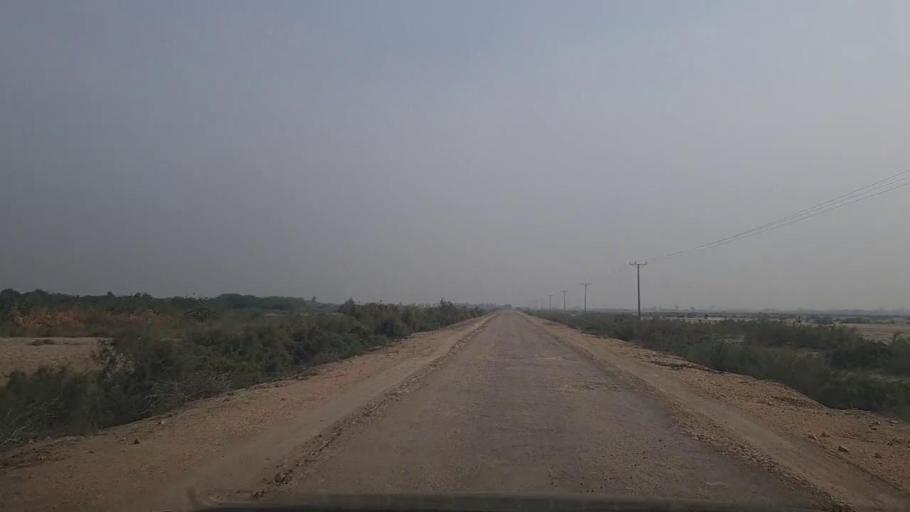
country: PK
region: Sindh
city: Mirpur Sakro
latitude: 24.4596
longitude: 67.6965
